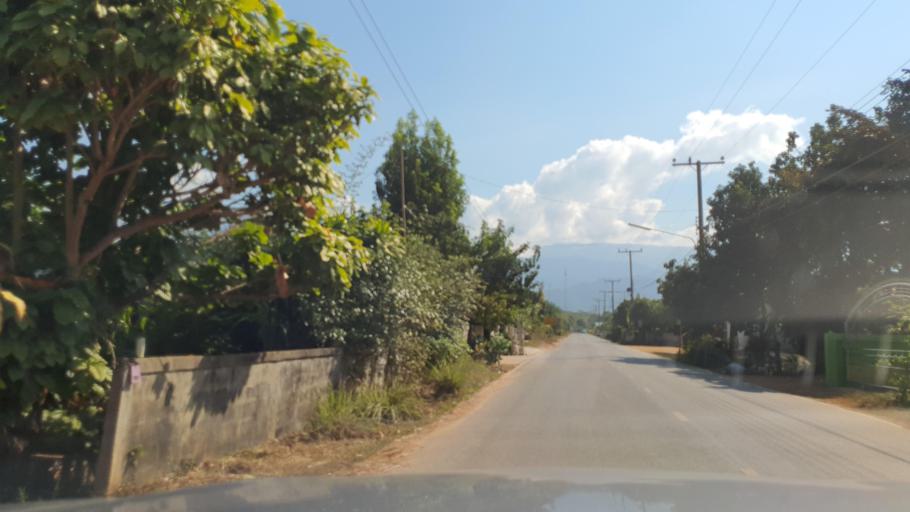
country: TH
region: Nan
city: Pua
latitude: 19.1451
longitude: 100.9212
